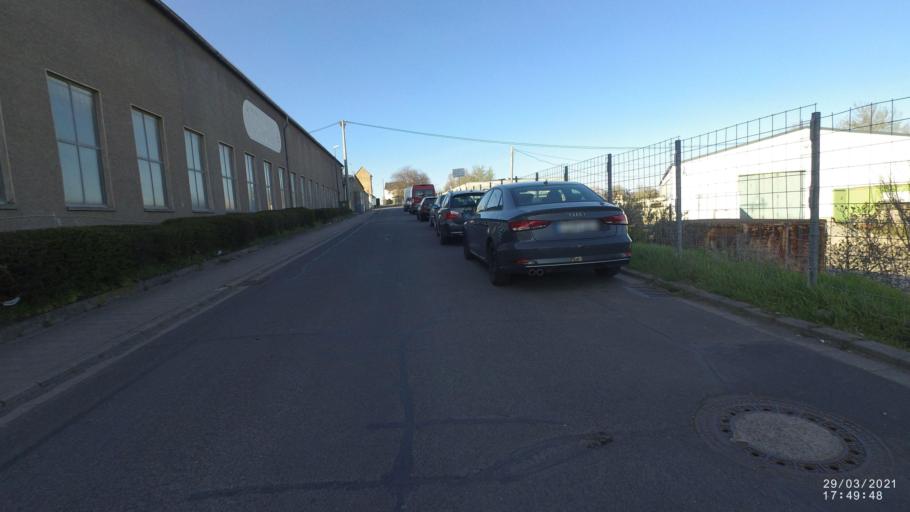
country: DE
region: Rheinland-Pfalz
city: Plaidt
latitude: 50.3984
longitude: 7.3940
